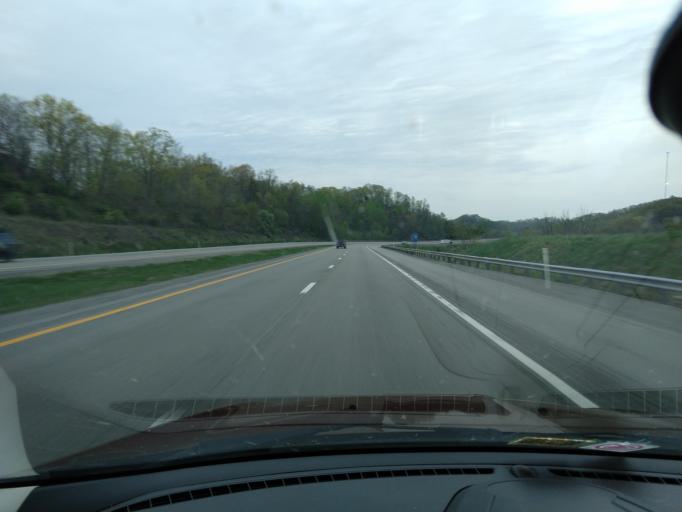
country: US
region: West Virginia
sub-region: Lewis County
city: Weston
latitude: 38.9509
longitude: -80.5343
